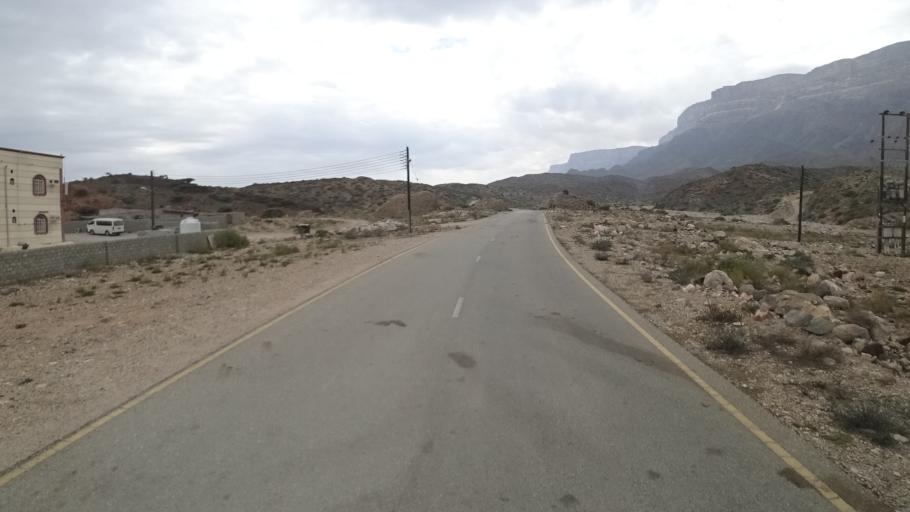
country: OM
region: Zufar
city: Salalah
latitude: 17.1730
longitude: 54.9620
